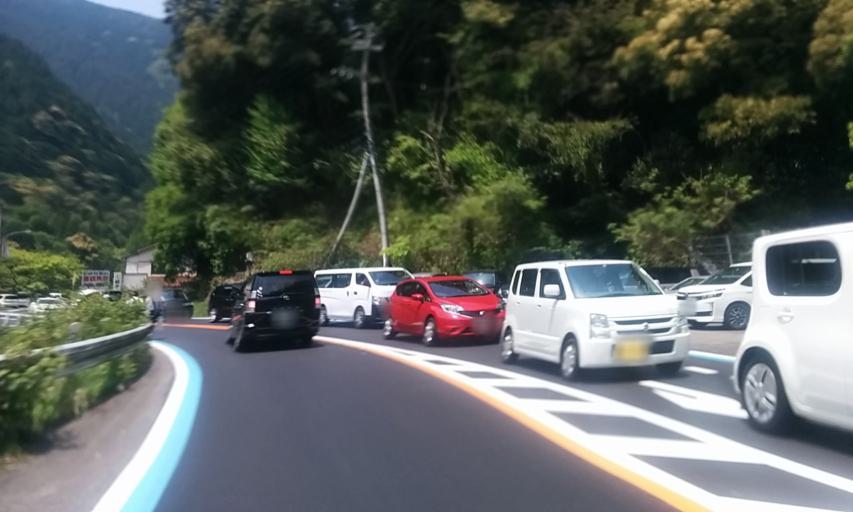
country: JP
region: Ehime
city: Niihama
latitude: 33.9038
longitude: 133.3108
